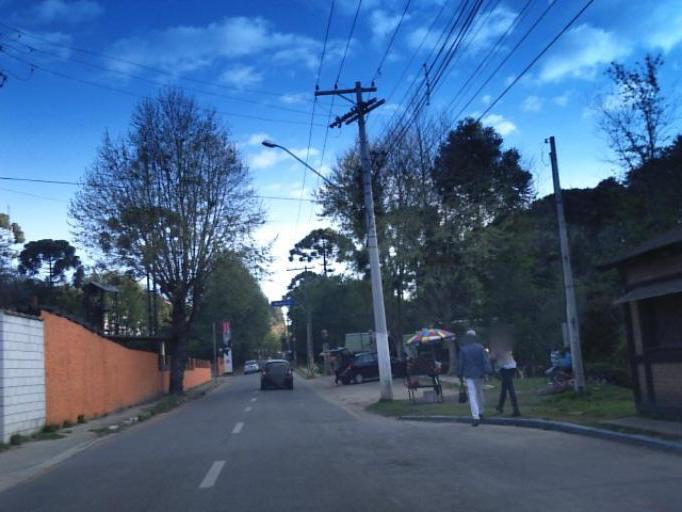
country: BR
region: Sao Paulo
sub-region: Campos Do Jordao
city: Campos do Jordao
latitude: -22.7209
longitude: -45.5743
